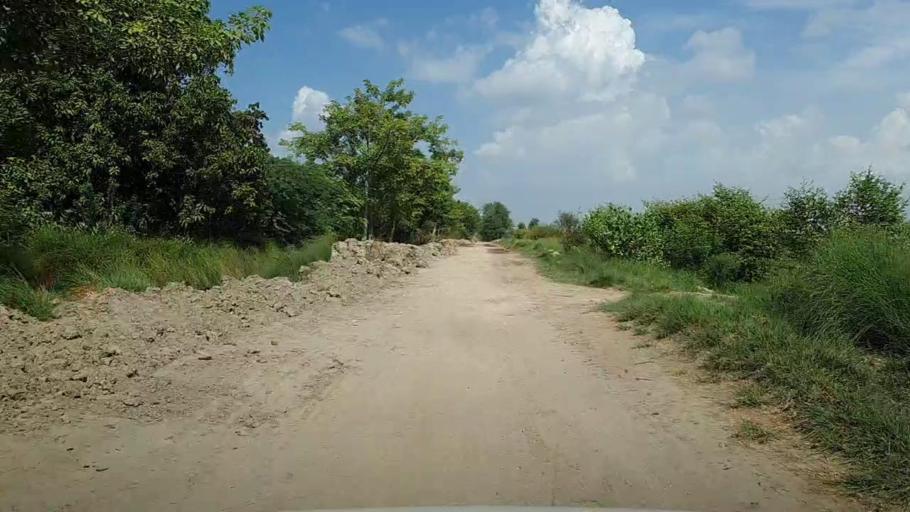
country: PK
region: Sindh
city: Bhiria
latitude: 26.9173
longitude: 68.2393
